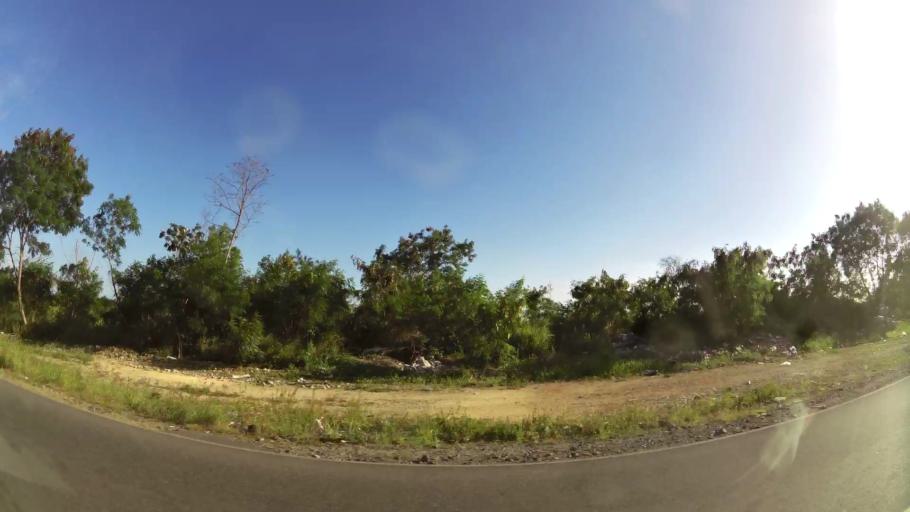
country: DO
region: Santo Domingo
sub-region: Santo Domingo
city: Santo Domingo Este
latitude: 18.4834
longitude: -69.8142
